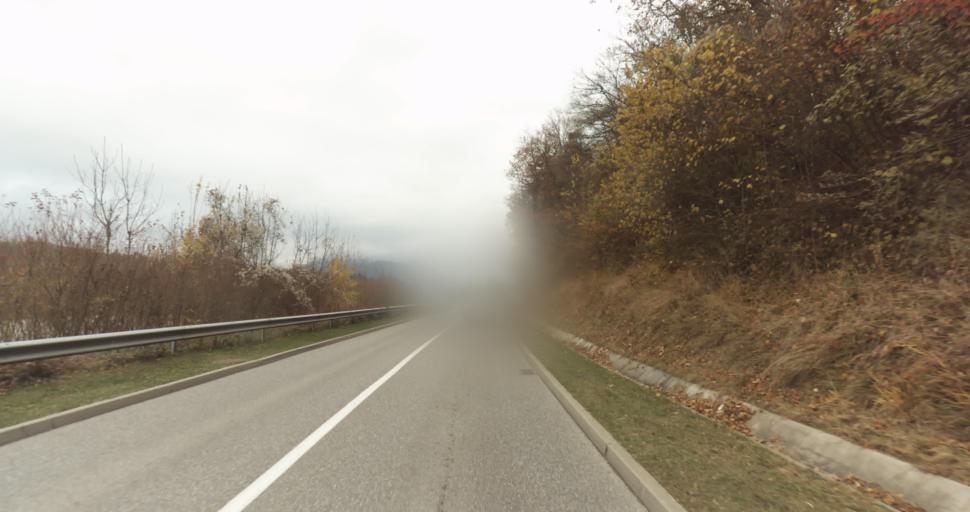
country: FR
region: Rhone-Alpes
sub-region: Departement de la Haute-Savoie
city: Saint-Martin-Bellevue
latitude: 45.9609
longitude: 6.1657
